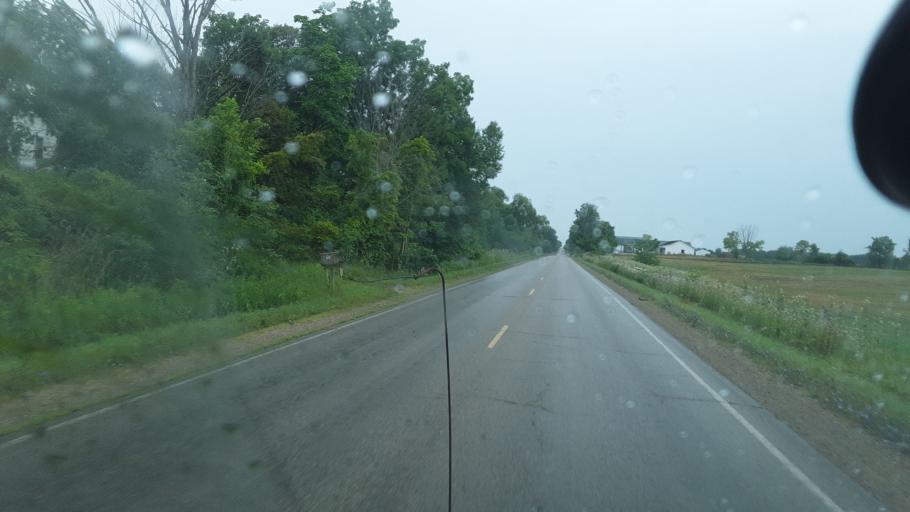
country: US
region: Michigan
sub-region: Hillsdale County
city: Reading
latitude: 41.7080
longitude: -84.7591
